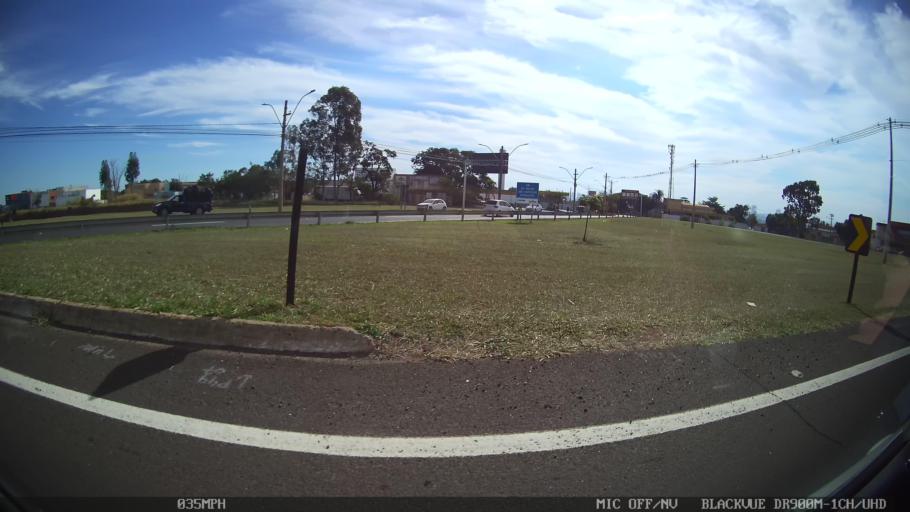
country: BR
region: Sao Paulo
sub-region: Araraquara
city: Araraquara
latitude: -21.8117
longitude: -48.1582
